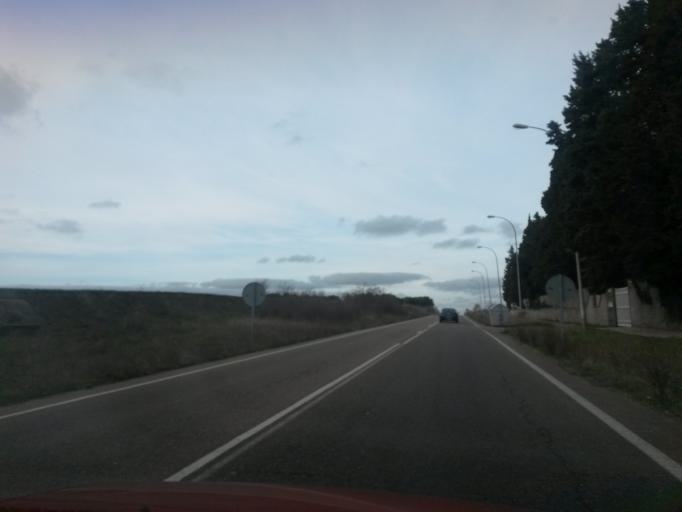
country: ES
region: Castille and Leon
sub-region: Provincia de Salamanca
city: Salamanca
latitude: 40.9835
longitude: -5.6603
